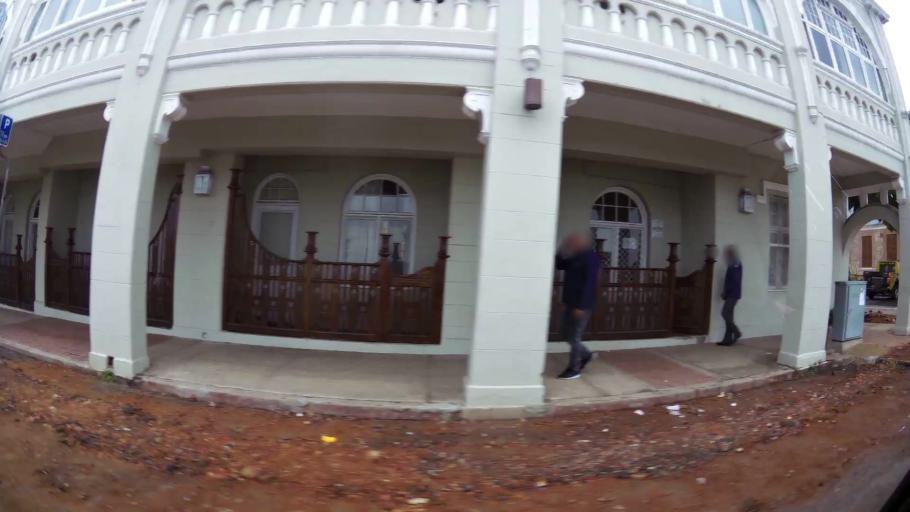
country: ZA
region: Eastern Cape
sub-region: Nelson Mandela Bay Metropolitan Municipality
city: Port Elizabeth
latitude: -33.9625
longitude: 25.6192
